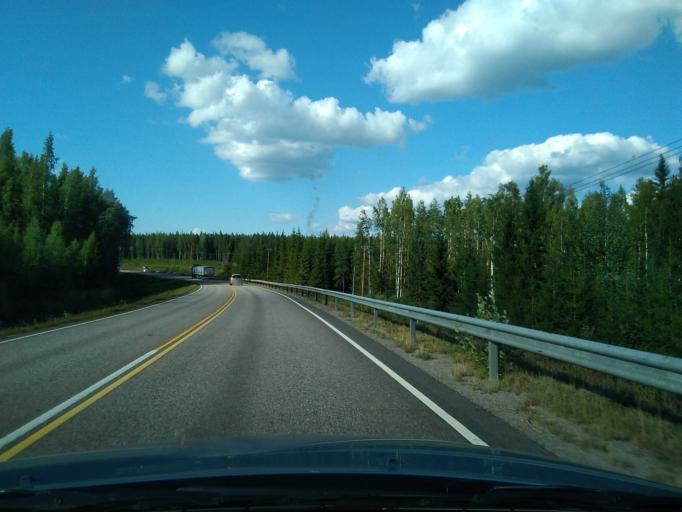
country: FI
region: Pirkanmaa
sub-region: Ylae-Pirkanmaa
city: Maenttae
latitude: 62.1169
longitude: 24.7447
